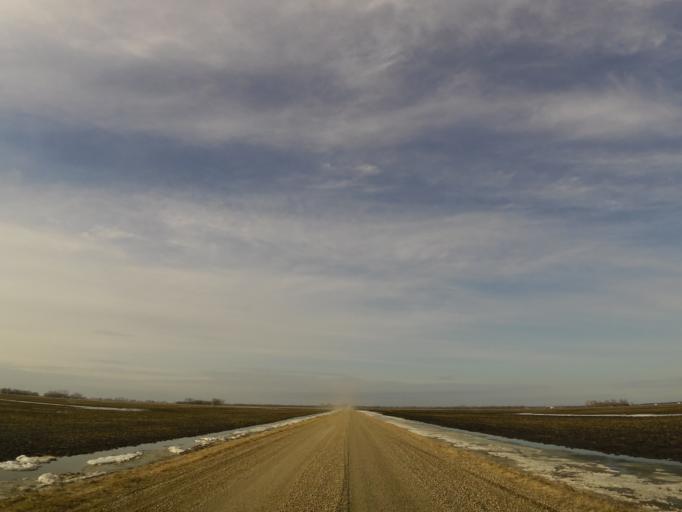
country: US
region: North Dakota
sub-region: Walsh County
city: Grafton
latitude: 48.4132
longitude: -97.2121
